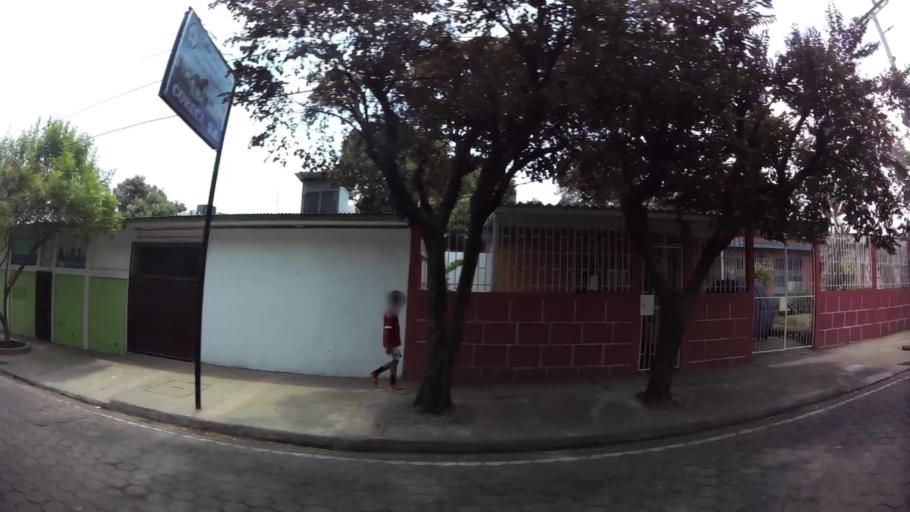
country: NI
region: Managua
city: Managua
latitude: 12.1215
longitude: -86.2975
